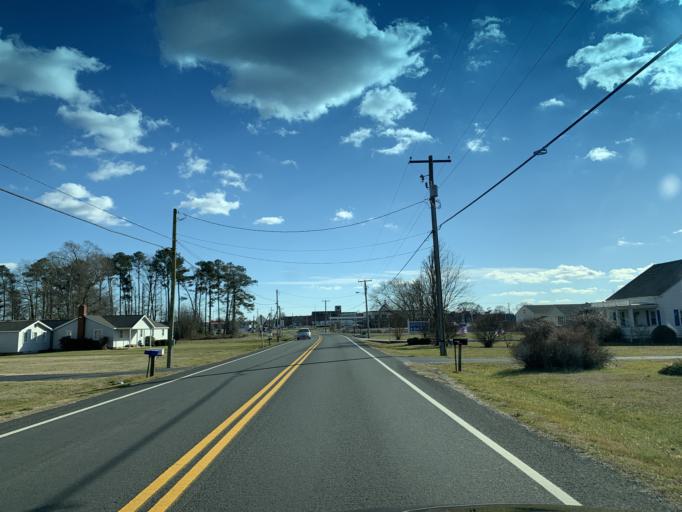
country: US
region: Maryland
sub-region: Worcester County
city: Berlin
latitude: 38.3458
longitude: -75.1915
